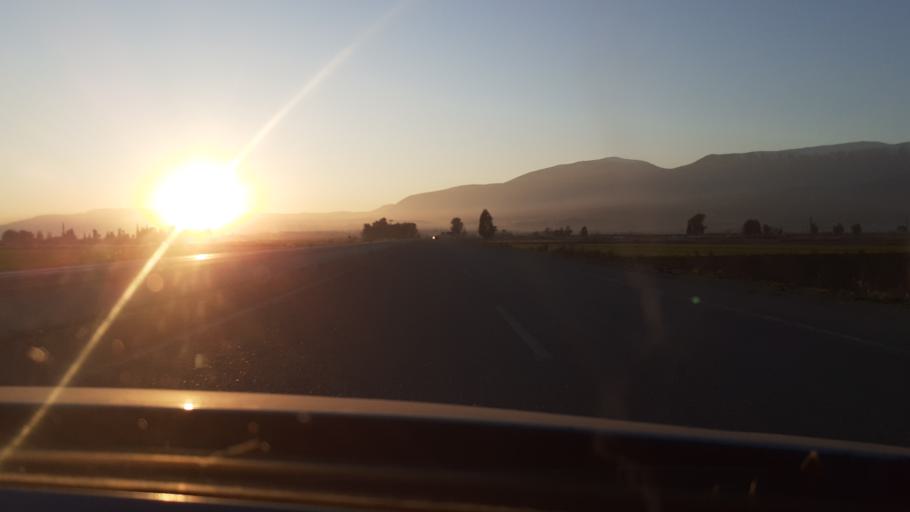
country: TR
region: Hatay
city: Kirikhan
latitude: 36.5065
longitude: 36.4257
